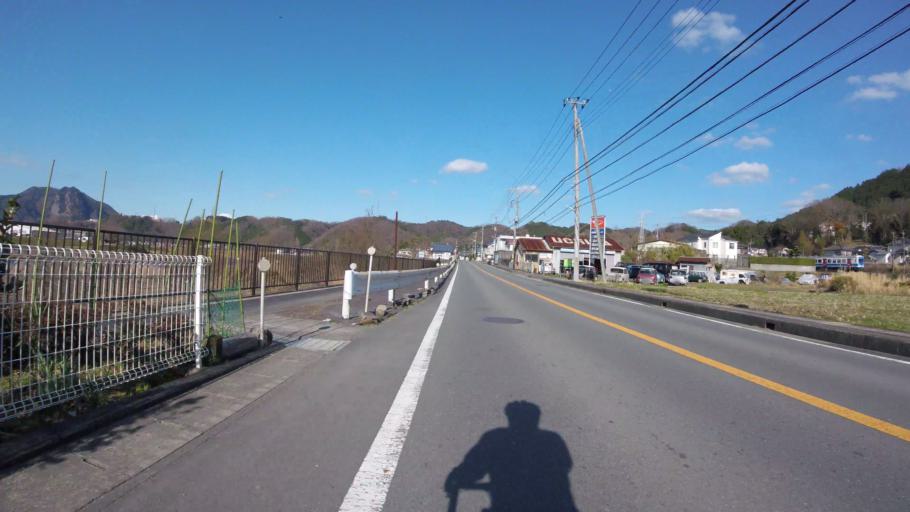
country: JP
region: Shizuoka
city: Ito
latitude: 34.9858
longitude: 138.9533
